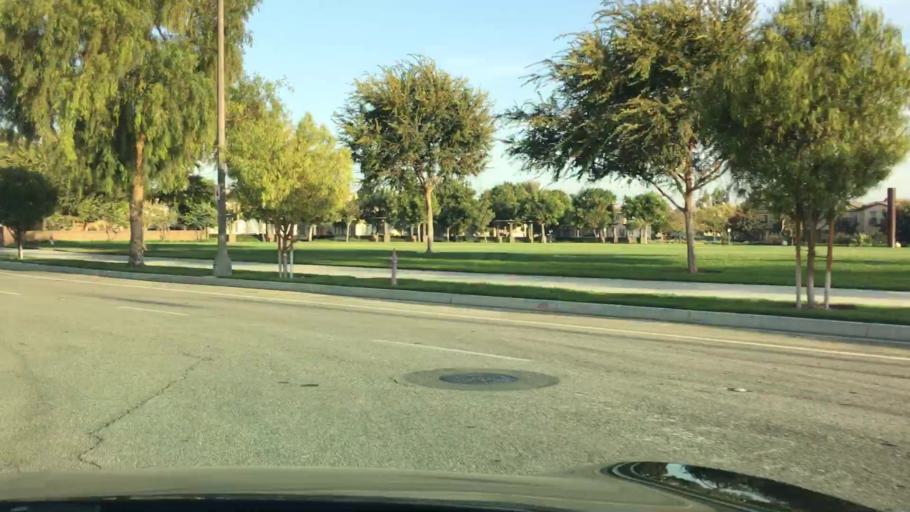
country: US
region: California
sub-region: San Bernardino County
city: Chino
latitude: 33.9902
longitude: -117.6542
